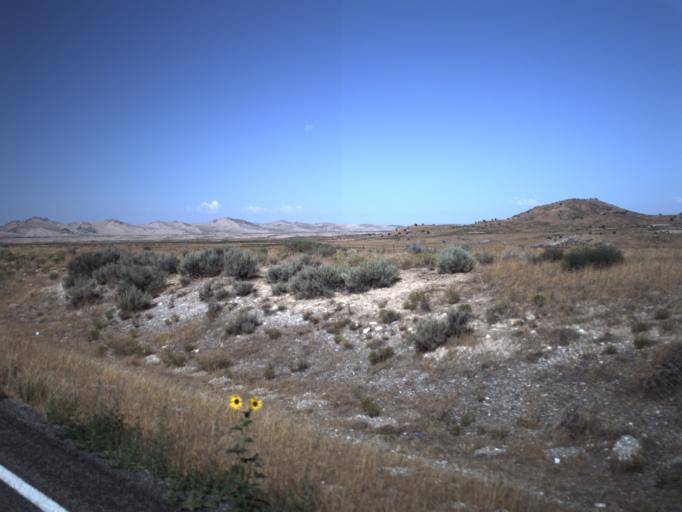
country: US
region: Utah
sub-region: Millard County
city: Delta
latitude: 39.6666
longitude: -112.2723
